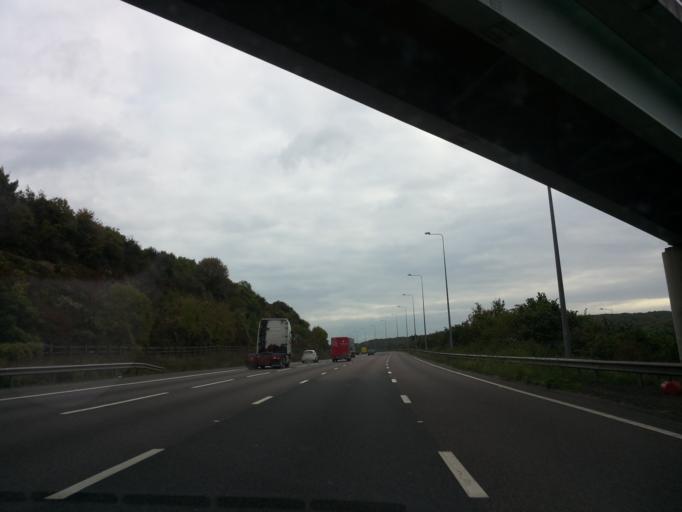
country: GB
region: England
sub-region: Medway
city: Rochester
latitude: 51.3564
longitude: 0.4950
